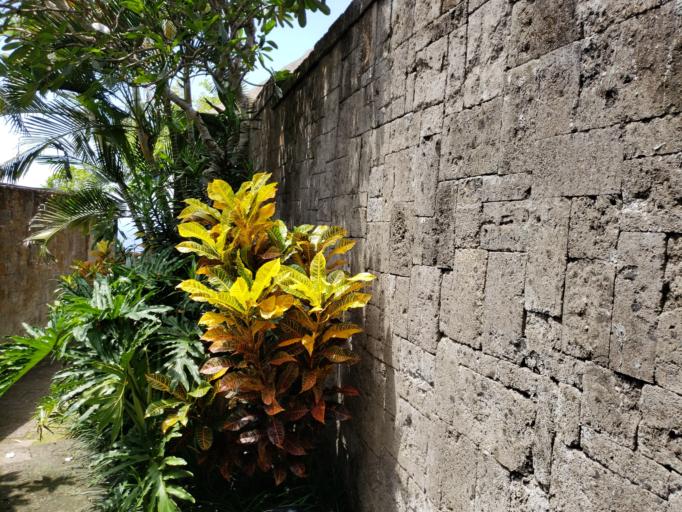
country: ID
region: Bali
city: Pecatu
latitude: -8.8448
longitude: 115.1195
